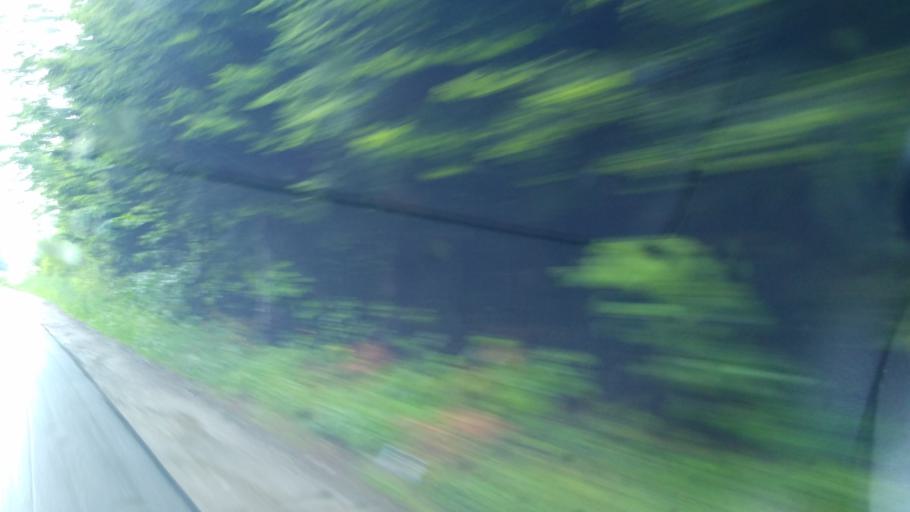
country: PL
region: Subcarpathian Voivodeship
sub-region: Powiat jasielski
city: Jaslo
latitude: 49.7888
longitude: 21.4916
